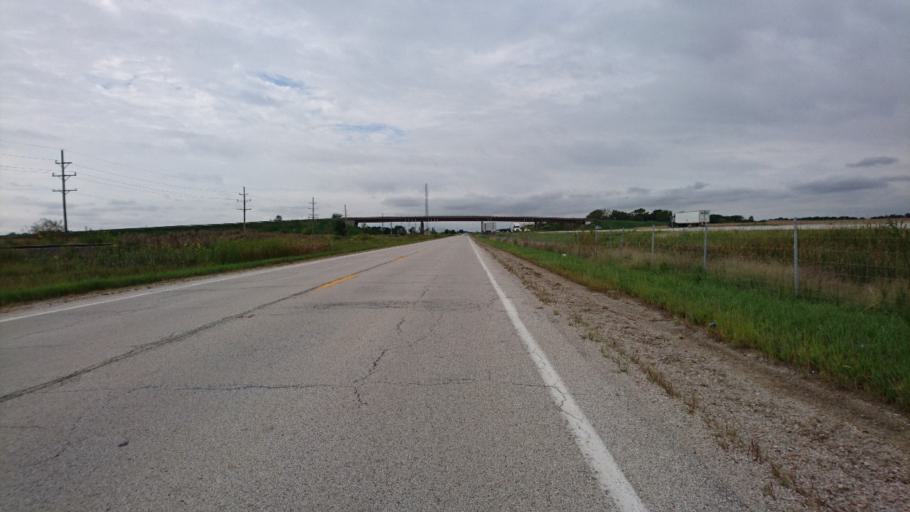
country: US
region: Illinois
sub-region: Livingston County
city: Dwight
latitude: 41.0669
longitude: -88.4606
